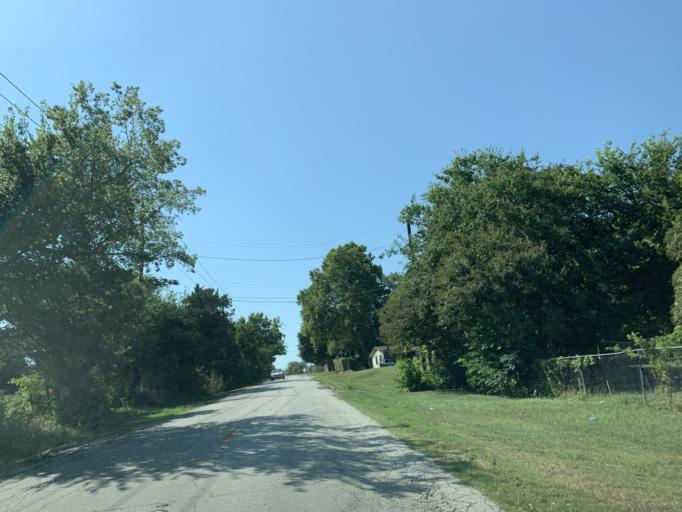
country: US
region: Texas
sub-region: Dallas County
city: Hutchins
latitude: 32.6717
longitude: -96.7459
